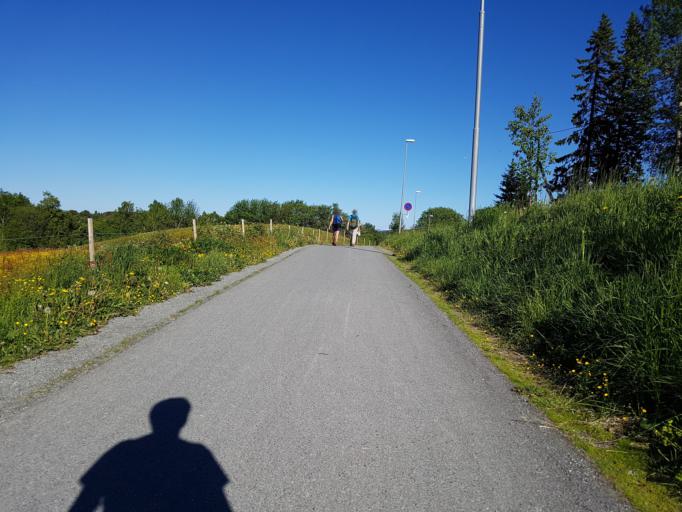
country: NO
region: Sor-Trondelag
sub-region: Trondheim
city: Trondheim
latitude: 63.4184
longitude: 10.3454
